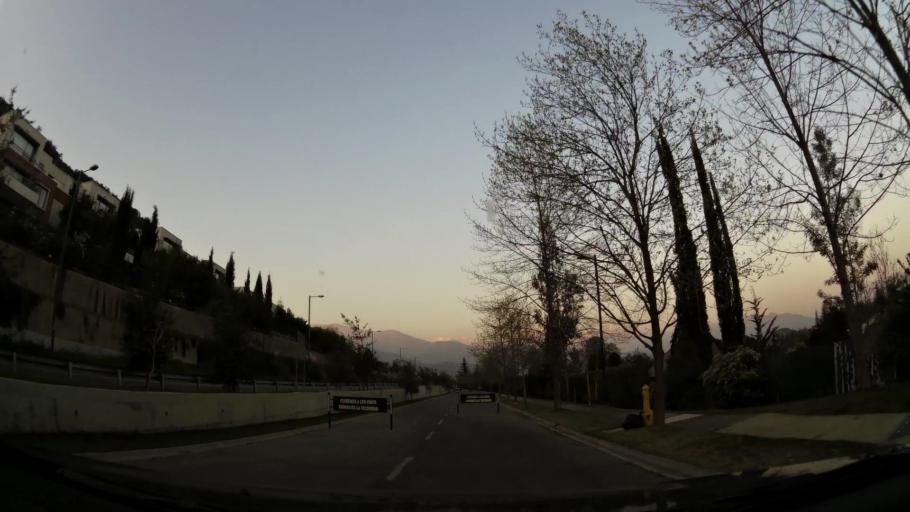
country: CL
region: Santiago Metropolitan
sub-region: Provincia de Chacabuco
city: Chicureo Abajo
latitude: -33.3363
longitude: -70.5610
